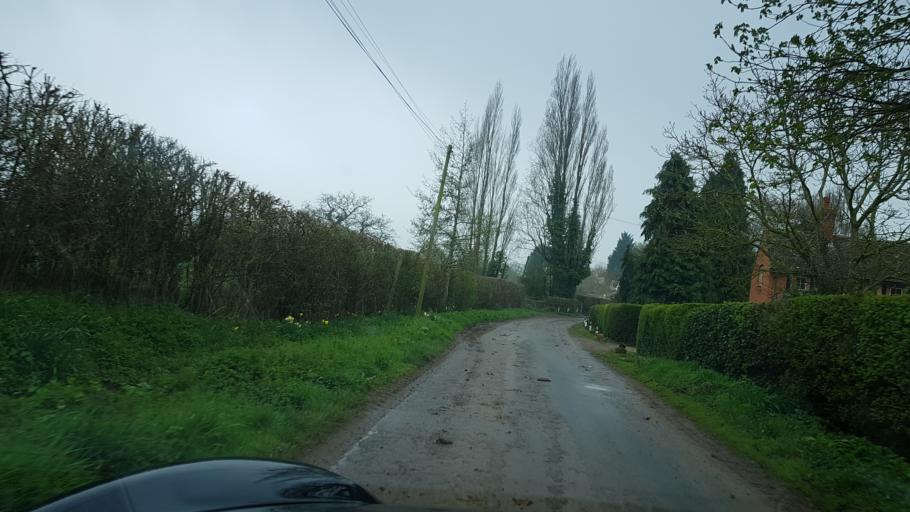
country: GB
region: England
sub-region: Herefordshire
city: Yatton
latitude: 52.0215
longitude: -2.5220
